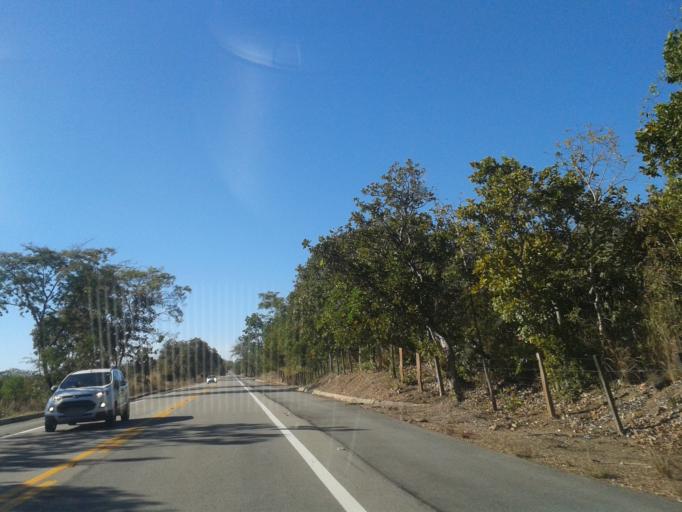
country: BR
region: Goias
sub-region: Itapuranga
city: Itapuranga
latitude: -15.3852
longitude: -50.3904
